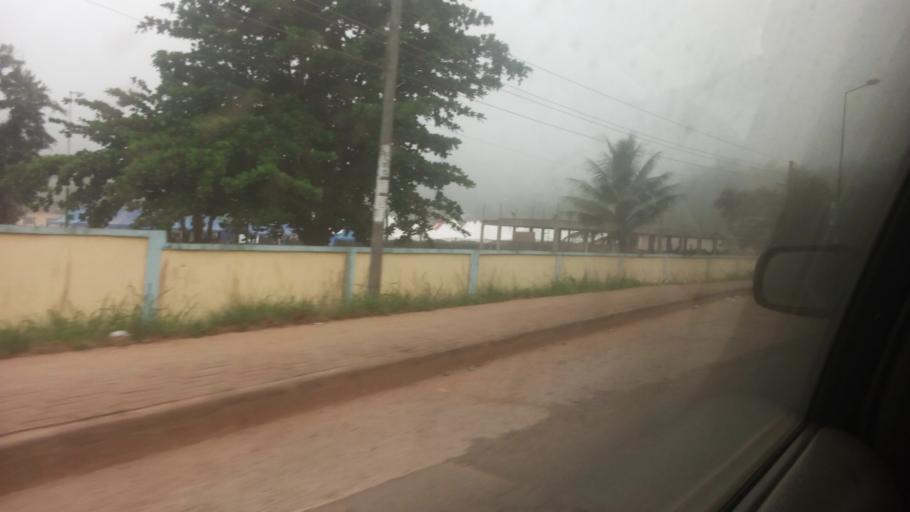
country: GH
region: Western
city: Tarkwa
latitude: 5.2910
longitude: -2.0029
